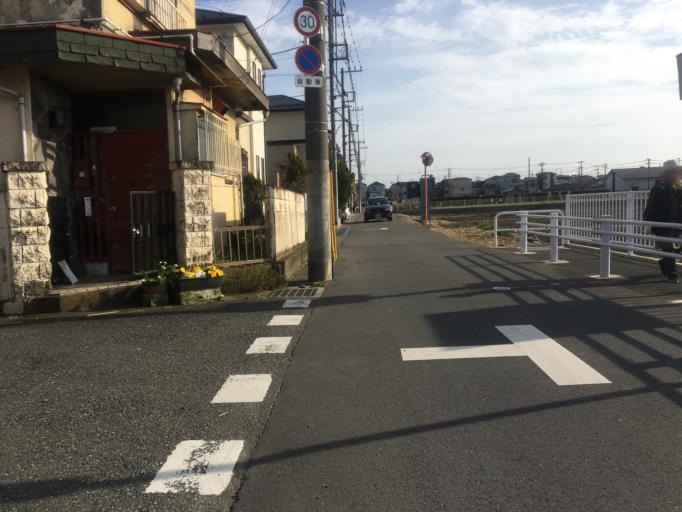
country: JP
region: Saitama
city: Shiki
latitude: 35.8405
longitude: 139.5725
